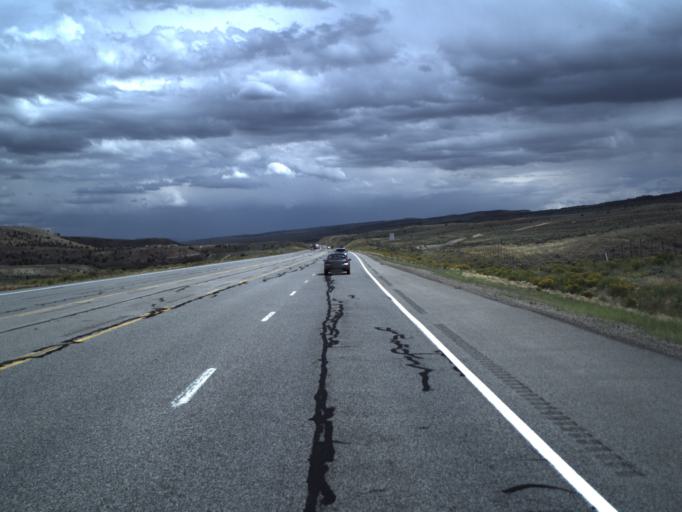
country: US
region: Utah
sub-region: Carbon County
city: Helper
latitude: 39.8416
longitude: -110.9903
